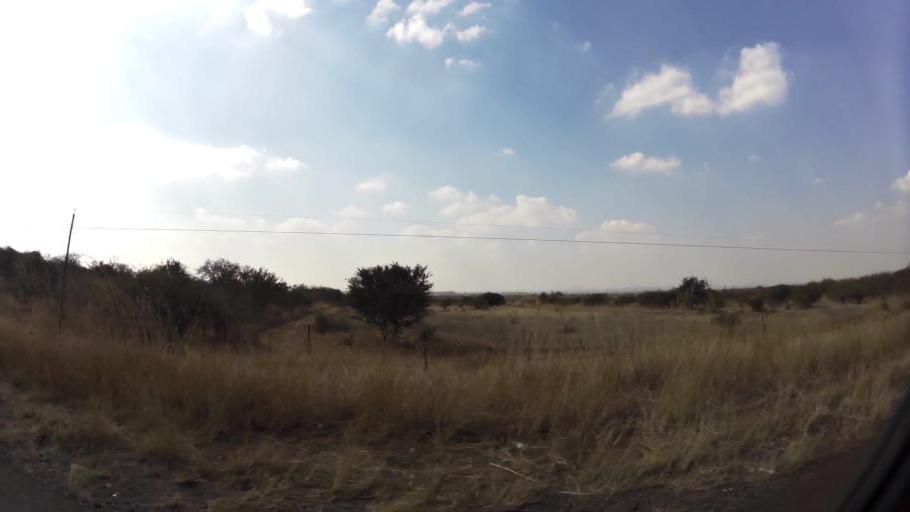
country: ZA
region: North-West
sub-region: Bojanala Platinum District Municipality
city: Rustenburg
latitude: -25.5304
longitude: 27.1152
